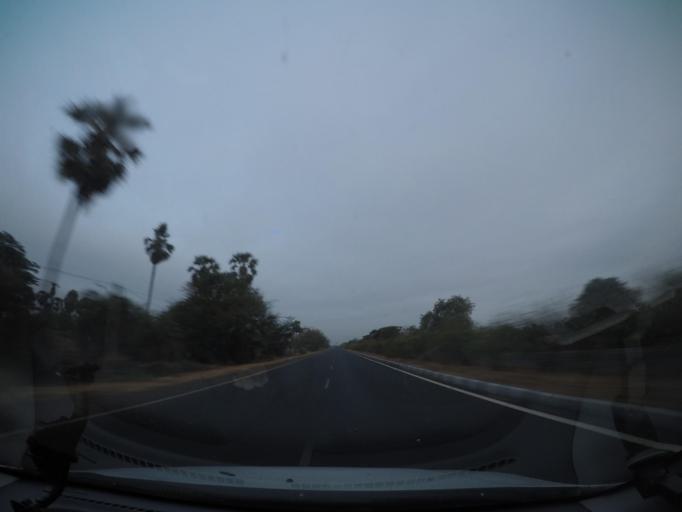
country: IN
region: Andhra Pradesh
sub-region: West Godavari
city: Tadepallegudem
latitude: 16.8101
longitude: 81.3421
